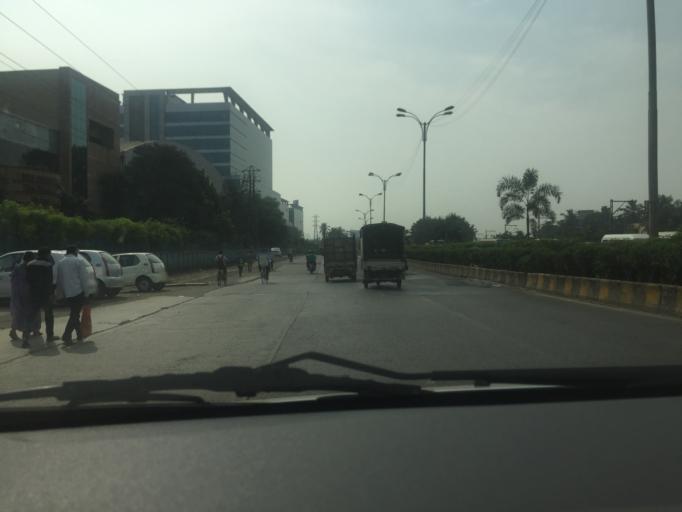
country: IN
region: Maharashtra
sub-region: Thane
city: Airoli
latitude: 19.1650
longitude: 72.9998
